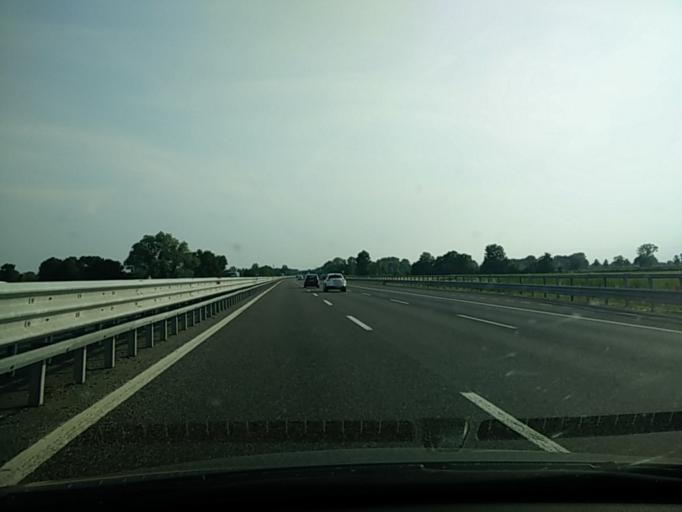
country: IT
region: Lombardy
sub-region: Citta metropolitana di Milano
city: Zibido San Giacomo
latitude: 45.3475
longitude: 9.1057
